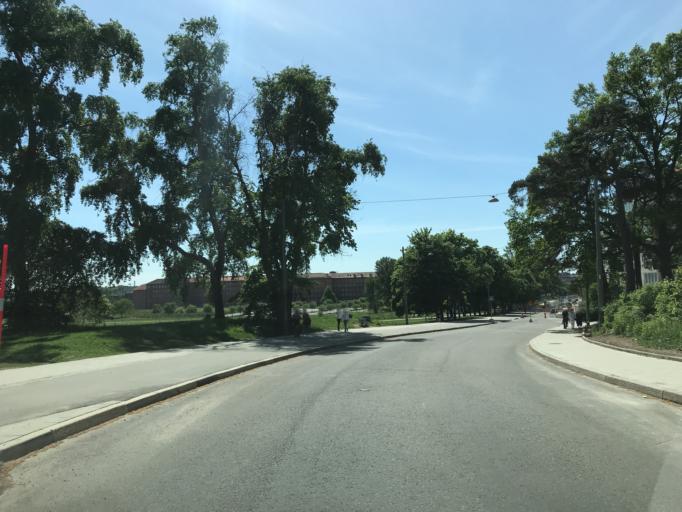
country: SE
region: Stockholm
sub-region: Stockholms Kommun
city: OEstermalm
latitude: 59.3452
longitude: 18.1016
